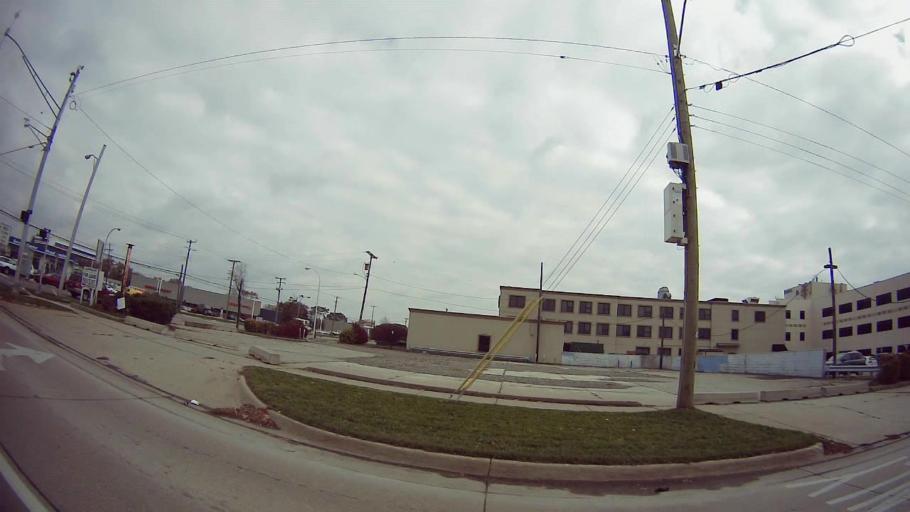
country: US
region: Michigan
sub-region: Oakland County
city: Madison Heights
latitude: 42.5054
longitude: -83.0675
